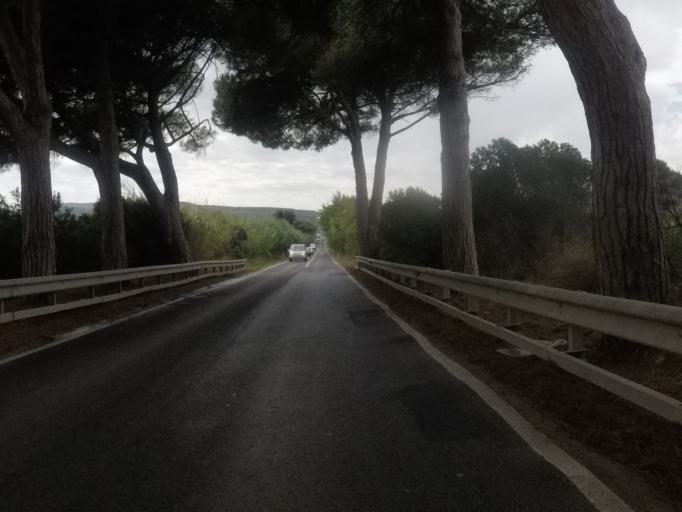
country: IT
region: Sardinia
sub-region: Provincia di Sassari
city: Sorso
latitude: 40.8326
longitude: 8.5950
